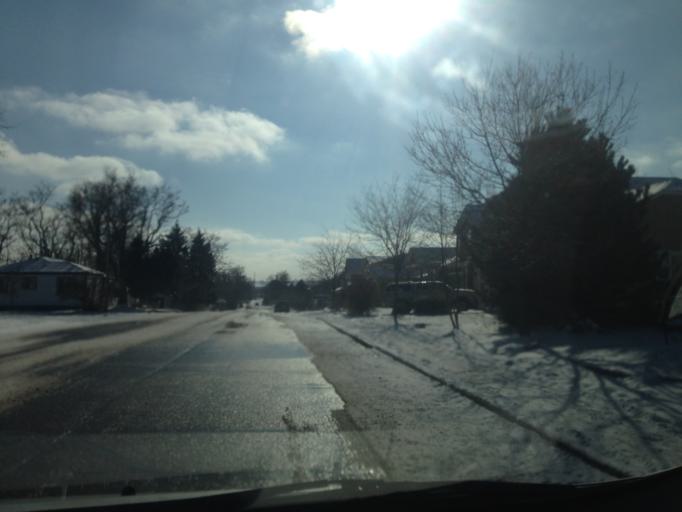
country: US
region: Colorado
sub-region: Boulder County
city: Lafayette
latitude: 39.9966
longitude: -105.0958
